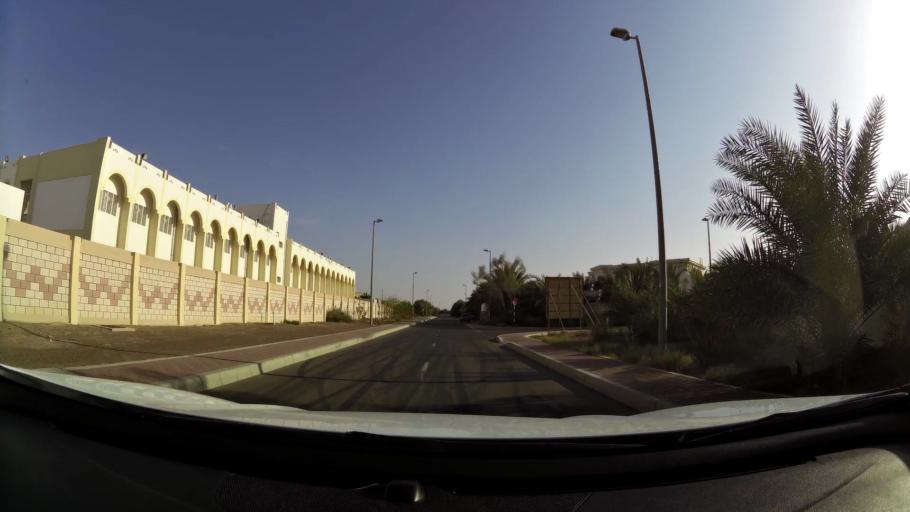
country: AE
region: Abu Dhabi
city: Al Ain
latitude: 24.0762
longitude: 55.8403
